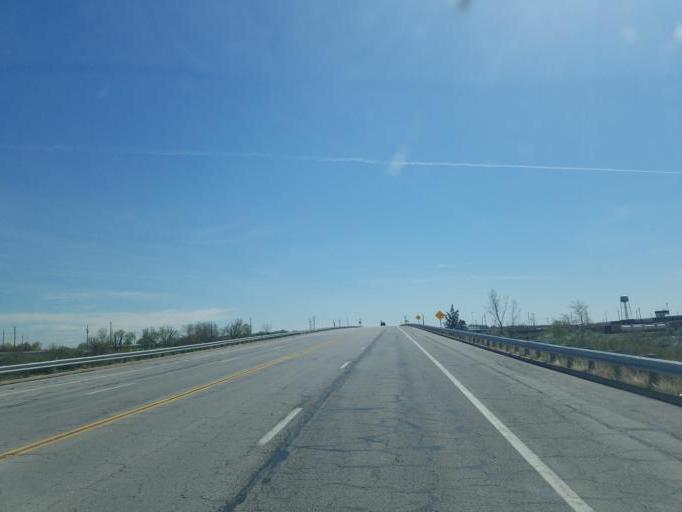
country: US
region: Ohio
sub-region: Huron County
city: Bellevue
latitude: 41.2974
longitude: -82.7799
